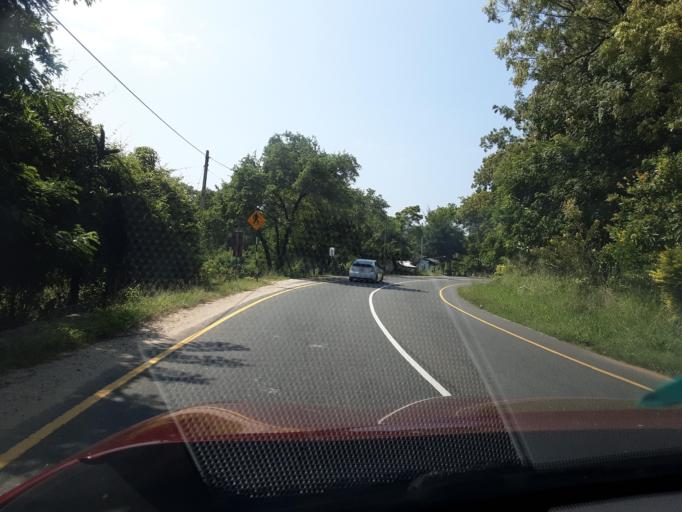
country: LK
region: Uva
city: Badulla
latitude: 7.2840
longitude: 81.0373
